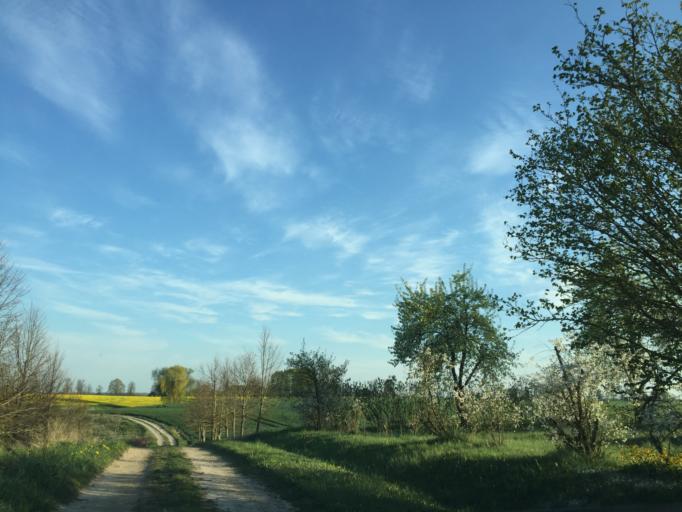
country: LV
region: Bauskas Rajons
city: Bauska
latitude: 56.3032
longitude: 24.2811
